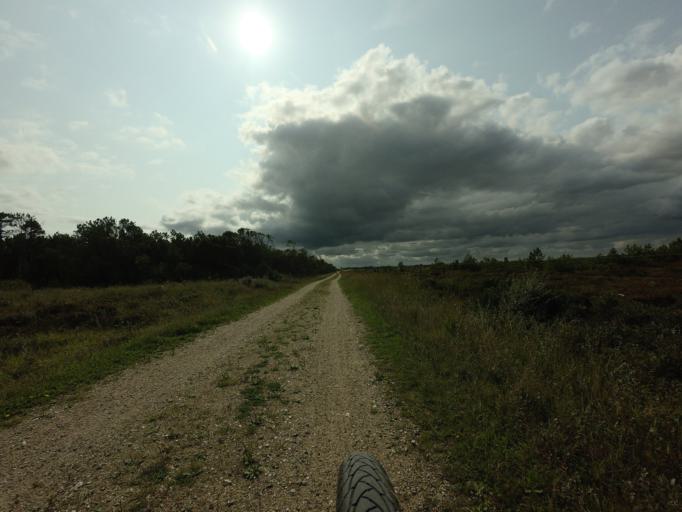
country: DK
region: North Denmark
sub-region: Frederikshavn Kommune
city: Strandby
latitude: 57.6390
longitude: 10.4003
